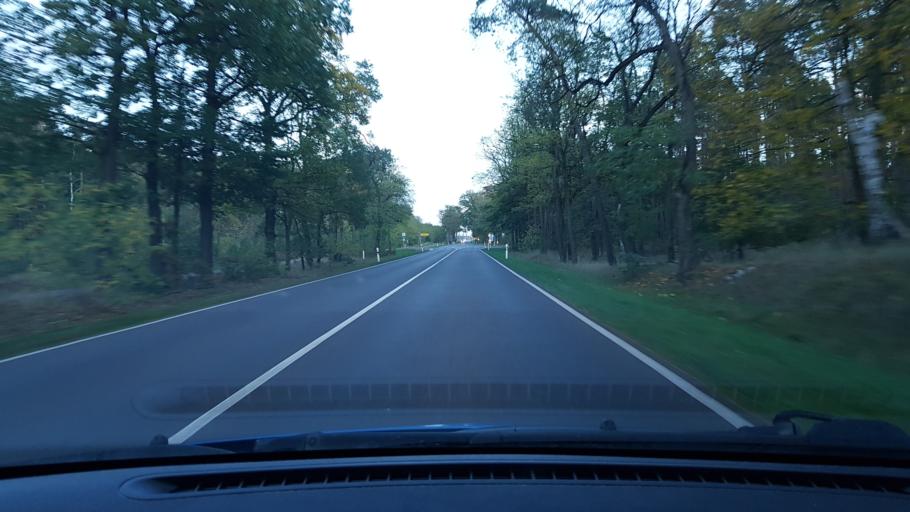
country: DE
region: Saxony-Anhalt
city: Wahlitz
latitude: 52.0899
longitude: 11.7991
